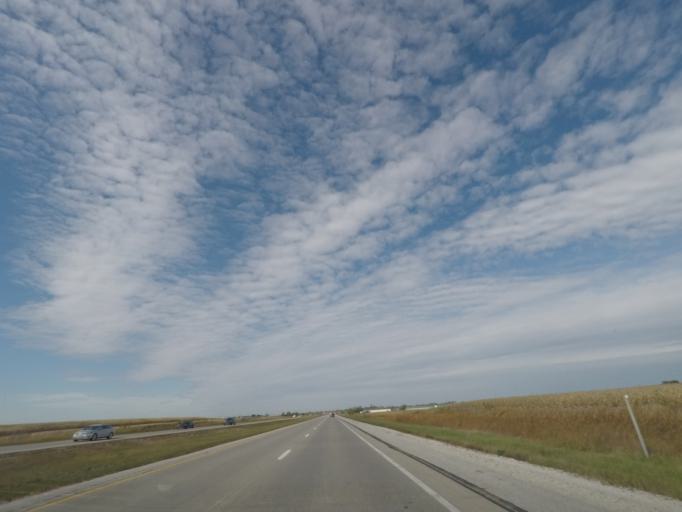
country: US
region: Iowa
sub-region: Story County
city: Ames
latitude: 42.0166
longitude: -93.7055
